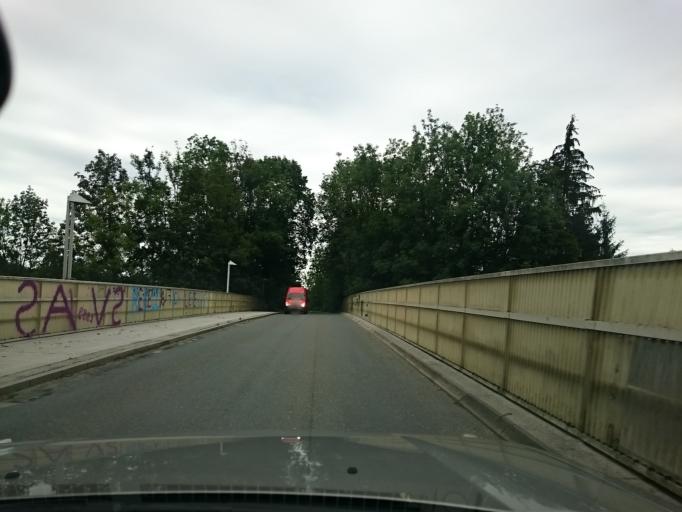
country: AT
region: Salzburg
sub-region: Politischer Bezirk Salzburg-Umgebung
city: Grodig
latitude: 47.7512
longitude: 13.0145
